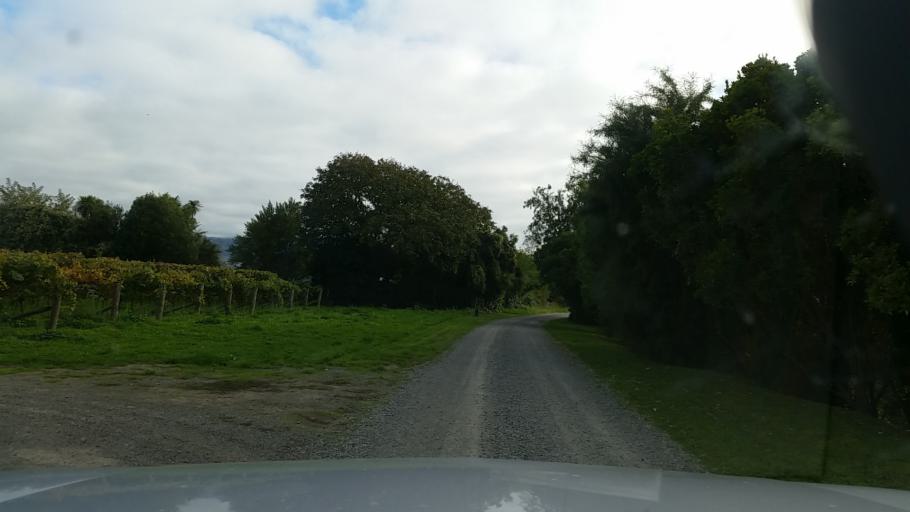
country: NZ
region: Marlborough
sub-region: Marlborough District
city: Blenheim
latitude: -41.4746
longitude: 173.9807
